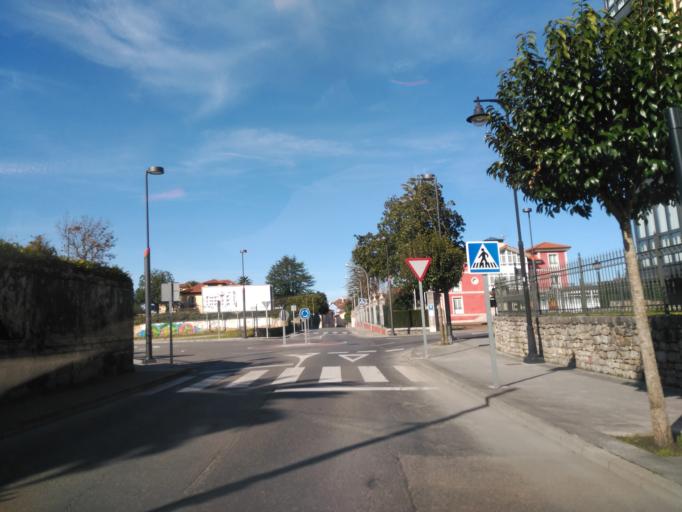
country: ES
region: Asturias
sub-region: Province of Asturias
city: Llanes
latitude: 43.4148
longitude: -4.7528
